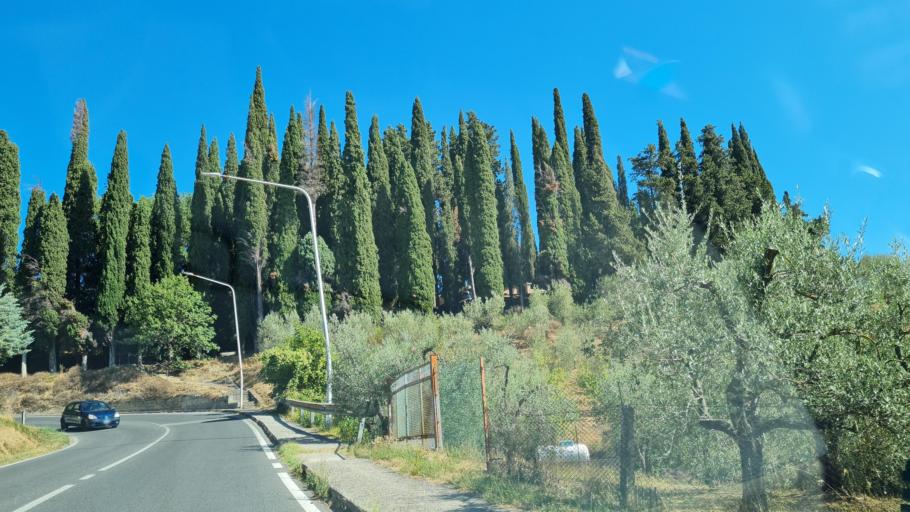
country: IT
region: Tuscany
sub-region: Provincia di Siena
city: Chianciano Terme
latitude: 43.0581
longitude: 11.8232
